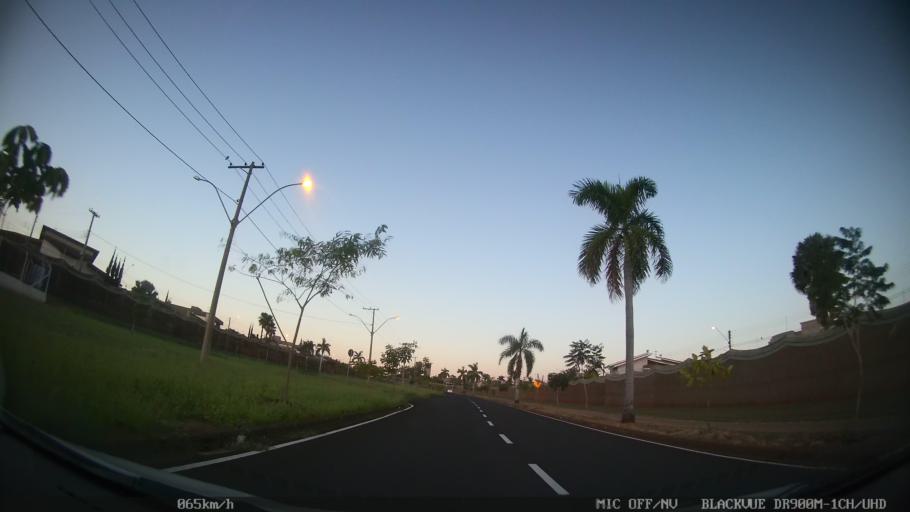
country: BR
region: Sao Paulo
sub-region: Sao Jose Do Rio Preto
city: Sao Jose do Rio Preto
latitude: -20.8168
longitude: -49.3423
